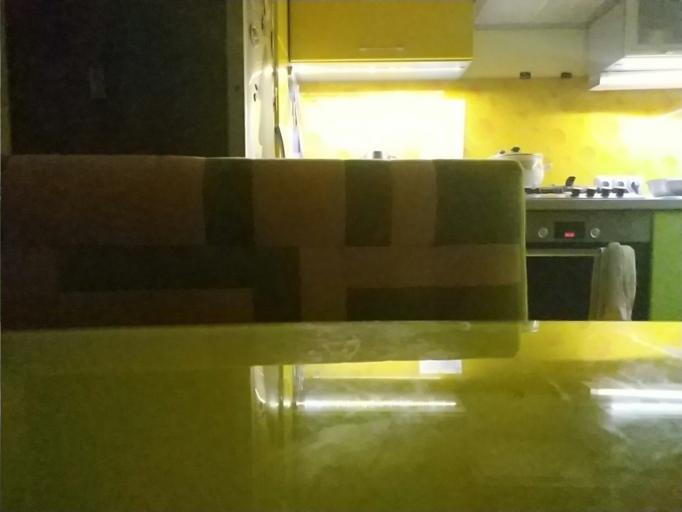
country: RU
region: Republic of Karelia
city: Kalevala
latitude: 65.3234
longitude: 30.6908
